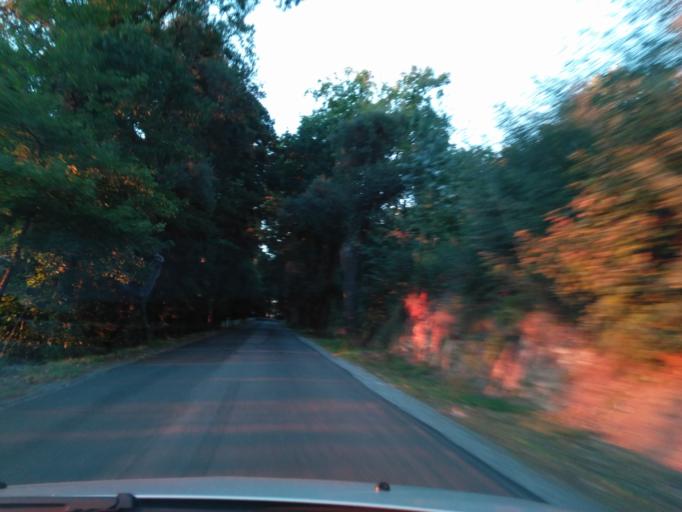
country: PT
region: Braga
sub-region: Braga
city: Adaufe
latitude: 41.5518
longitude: -8.3795
